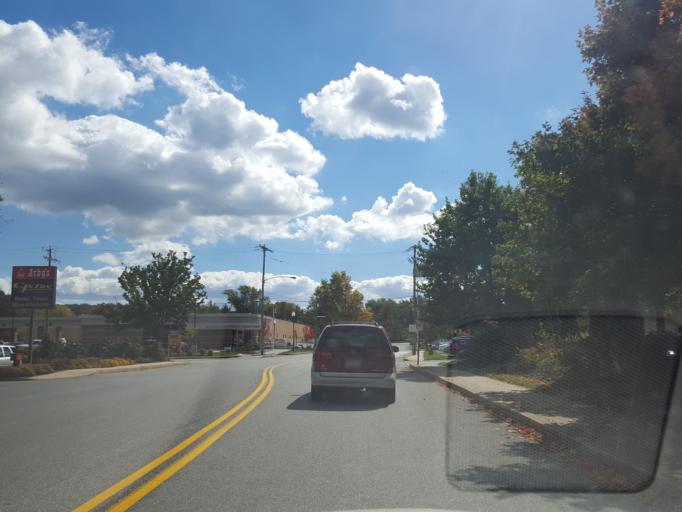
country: US
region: Pennsylvania
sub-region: York County
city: East York
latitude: 39.9744
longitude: -76.6730
